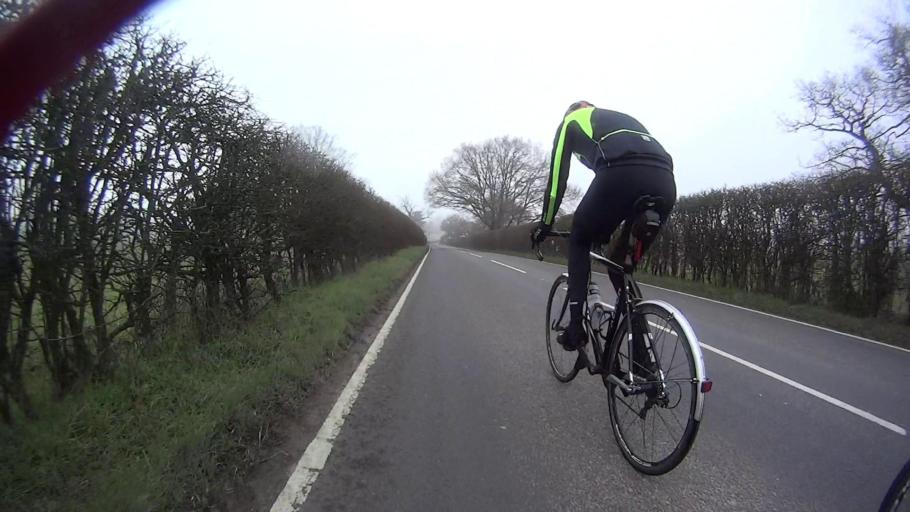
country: GB
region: England
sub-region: Surrey
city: Ockley
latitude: 51.1533
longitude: -0.3614
